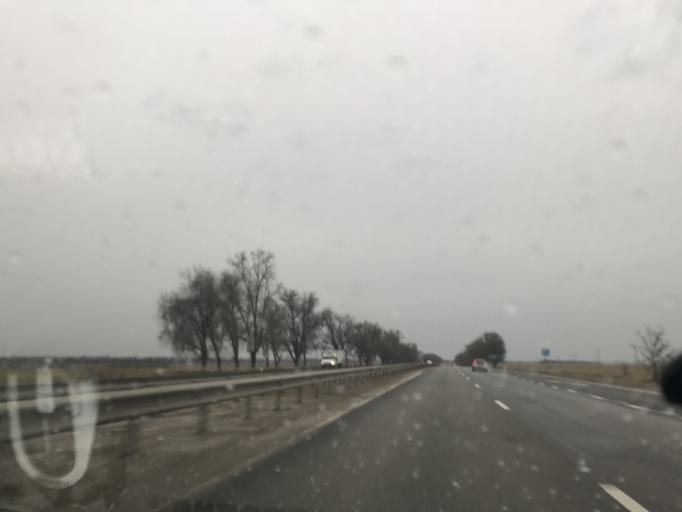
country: RU
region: Krasnodarskiy
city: Pavlovskaya
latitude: 46.1629
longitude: 39.8431
